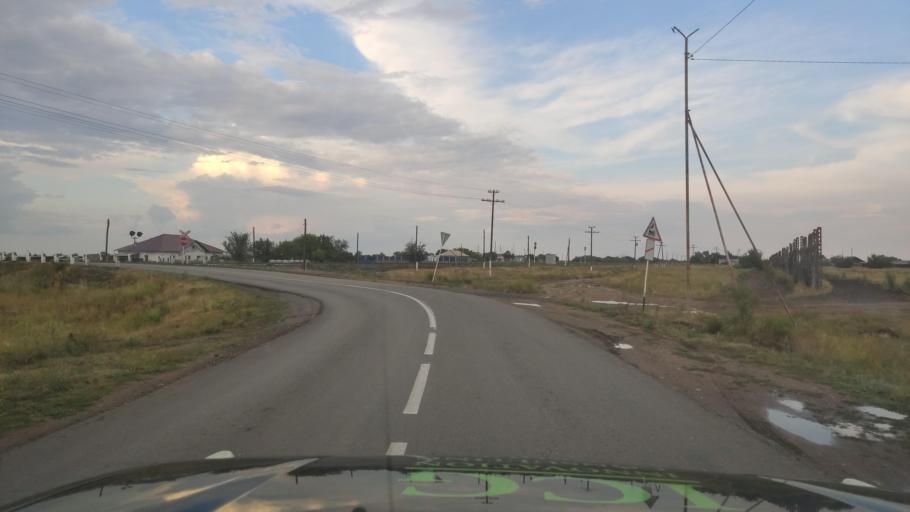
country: KZ
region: Pavlodar
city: Pavlodar
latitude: 52.3451
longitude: 77.2532
